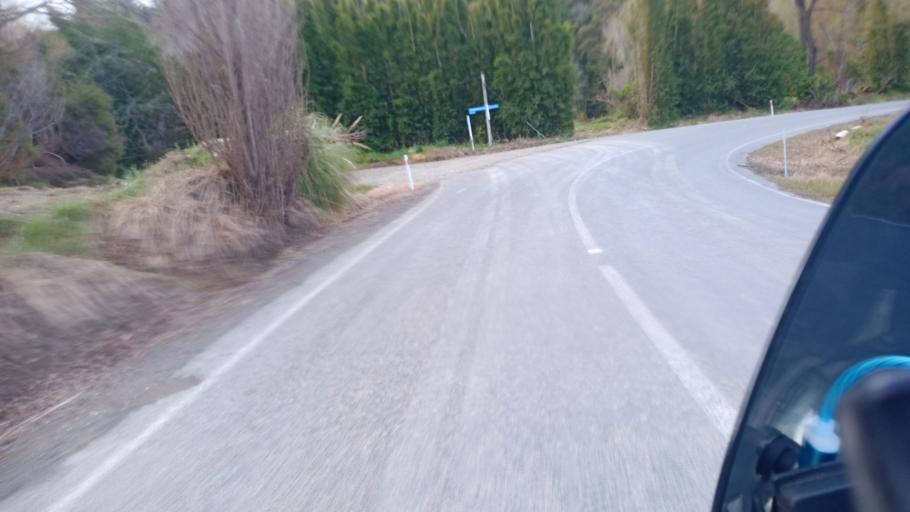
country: NZ
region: Gisborne
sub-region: Gisborne District
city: Gisborne
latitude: -38.2999
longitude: 178.2567
